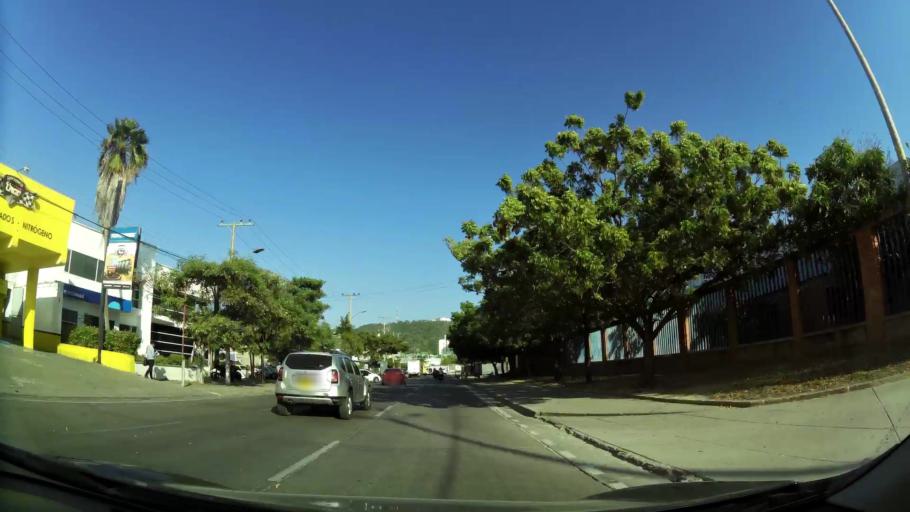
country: CO
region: Bolivar
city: Cartagena
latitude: 10.4197
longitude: -75.5387
